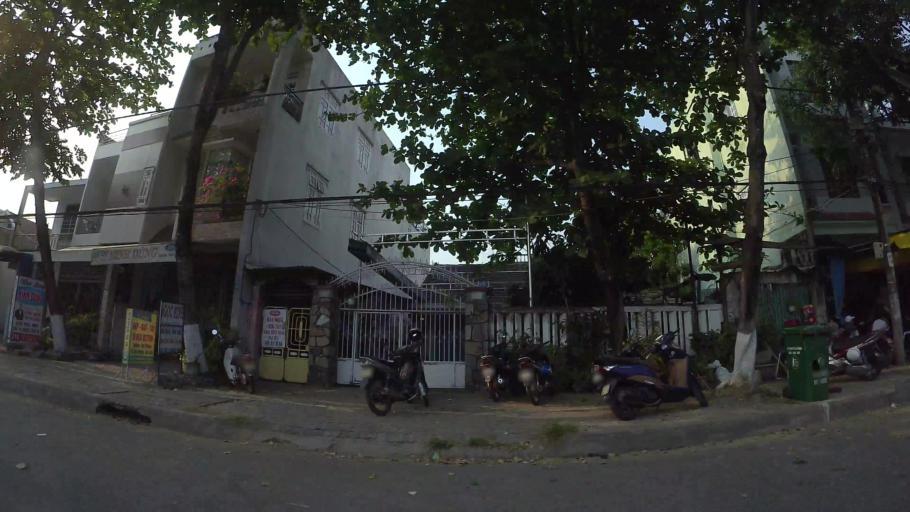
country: VN
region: Da Nang
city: Cam Le
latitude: 16.0165
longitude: 108.2027
